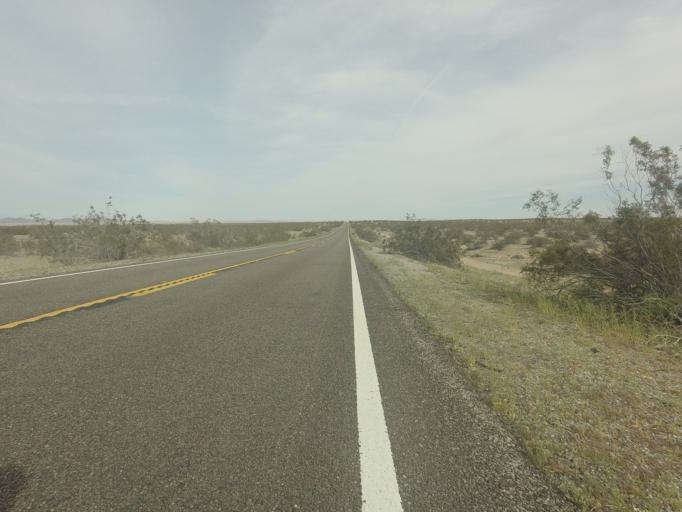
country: US
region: California
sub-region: Imperial County
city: Holtville
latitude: 32.9705
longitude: -115.2745
